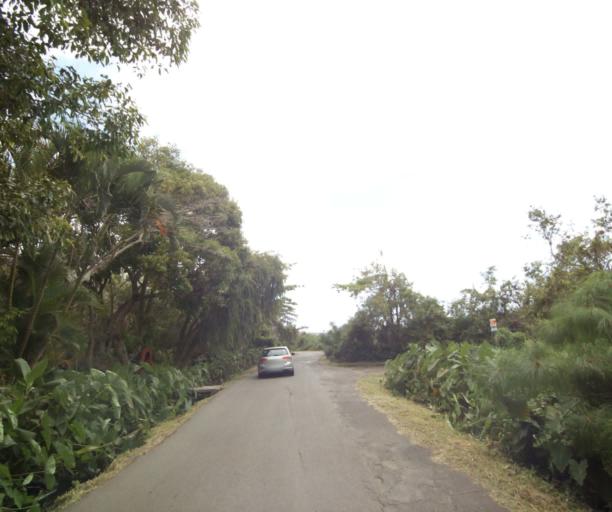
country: RE
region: Reunion
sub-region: Reunion
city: Saint-Paul
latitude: -20.9989
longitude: 55.3028
